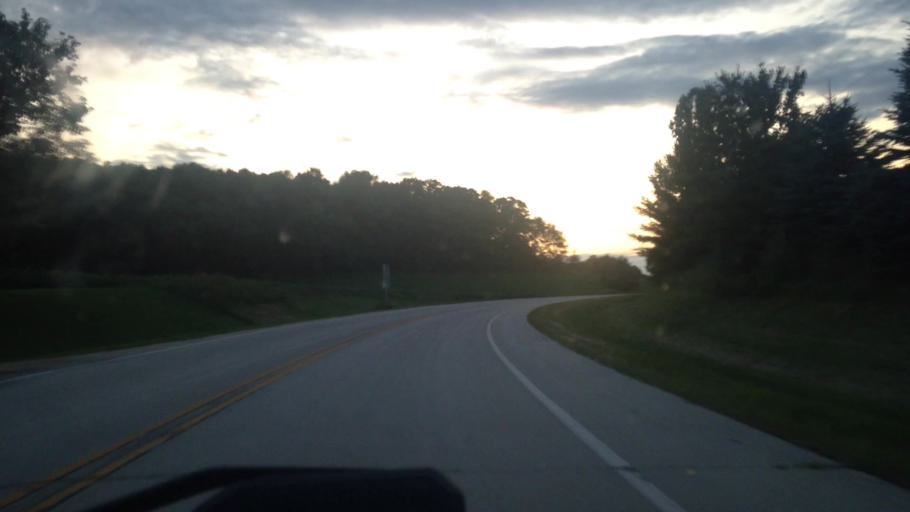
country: US
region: Wisconsin
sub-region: Dodge County
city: Mayville
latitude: 43.4778
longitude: -88.5060
